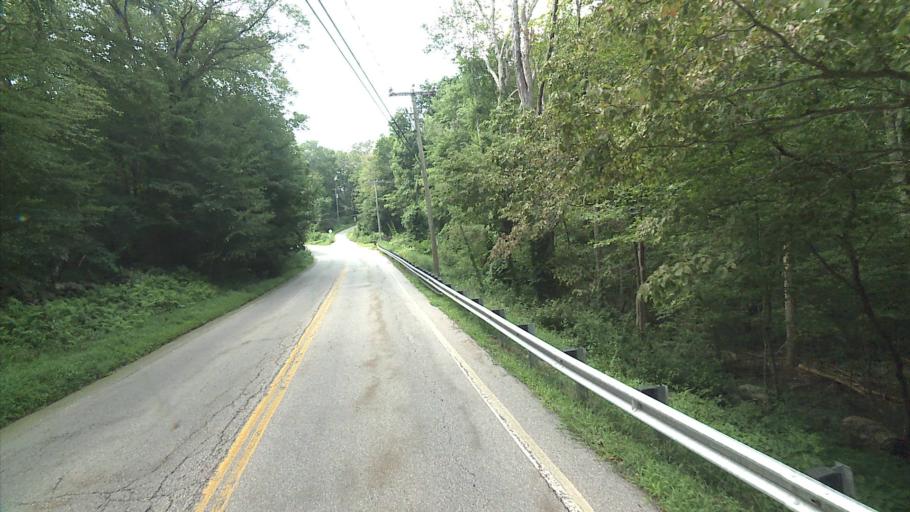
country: US
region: Connecticut
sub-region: Middlesex County
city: Essex Village
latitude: 41.4310
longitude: -72.3584
